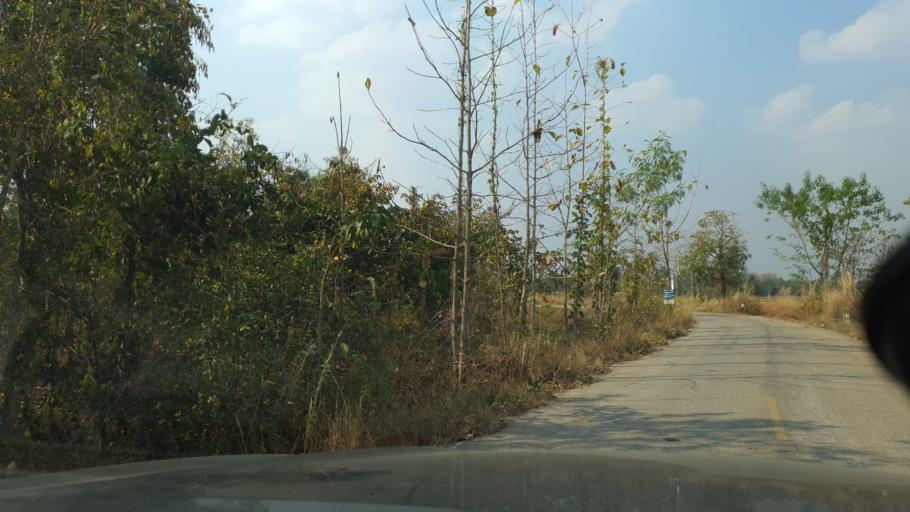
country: TH
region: Sukhothai
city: Ban Dan Lan Hoi
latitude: 17.0199
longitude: 99.5574
